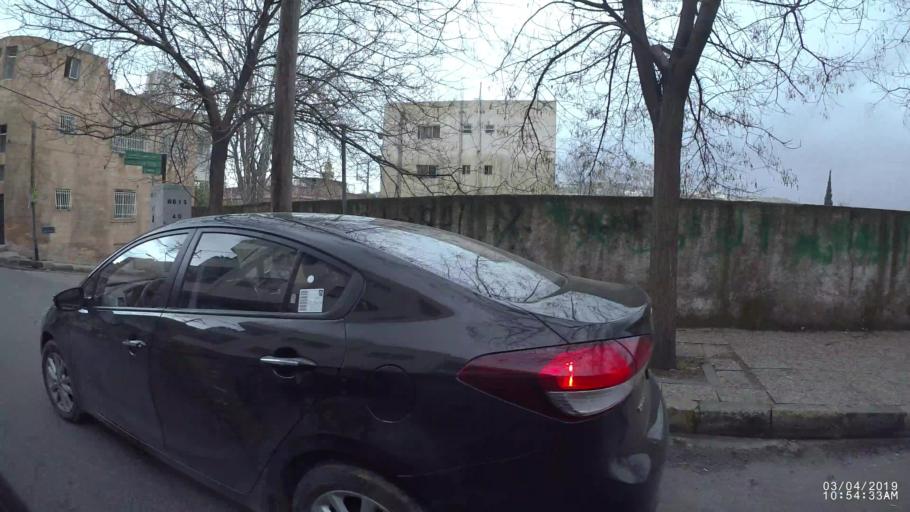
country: JO
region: Amman
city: Wadi as Sir
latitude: 31.9500
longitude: 35.8186
